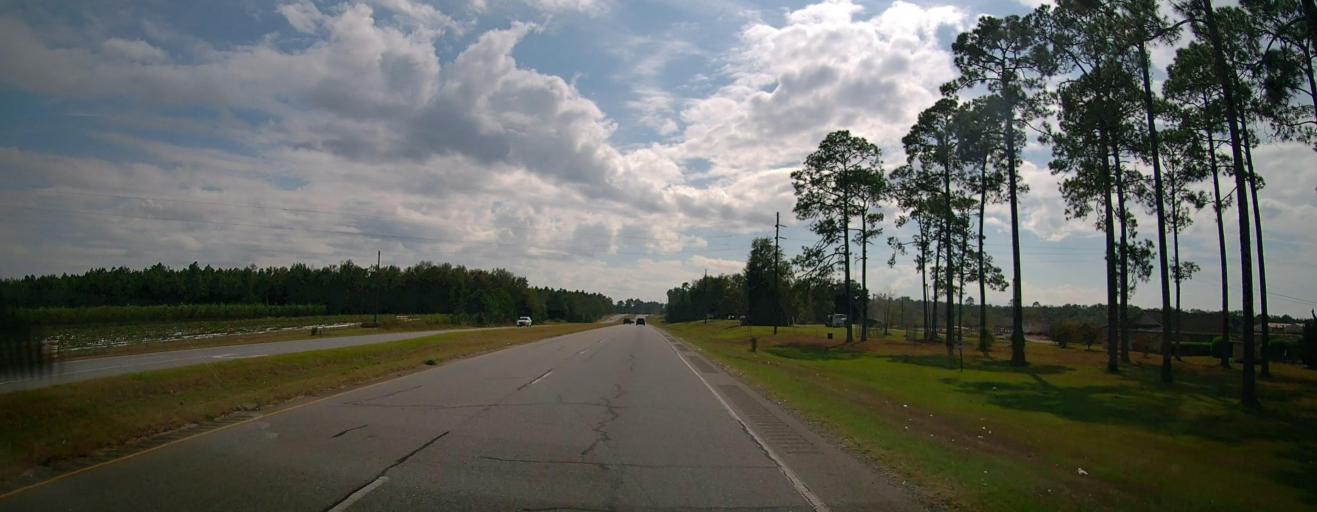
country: US
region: Georgia
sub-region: Mitchell County
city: Camilla
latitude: 31.3247
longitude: -84.1730
